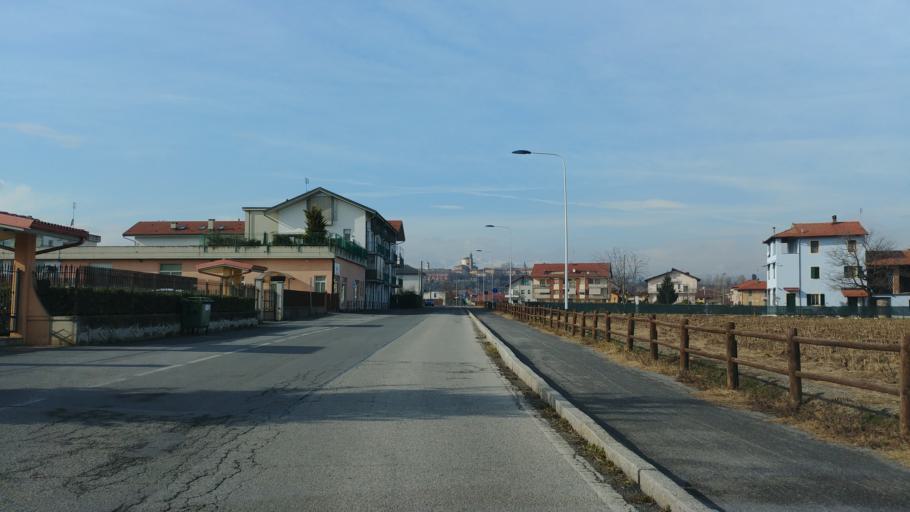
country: IT
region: Piedmont
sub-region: Provincia di Cuneo
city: Cuneo
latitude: 44.3932
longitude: 7.5669
